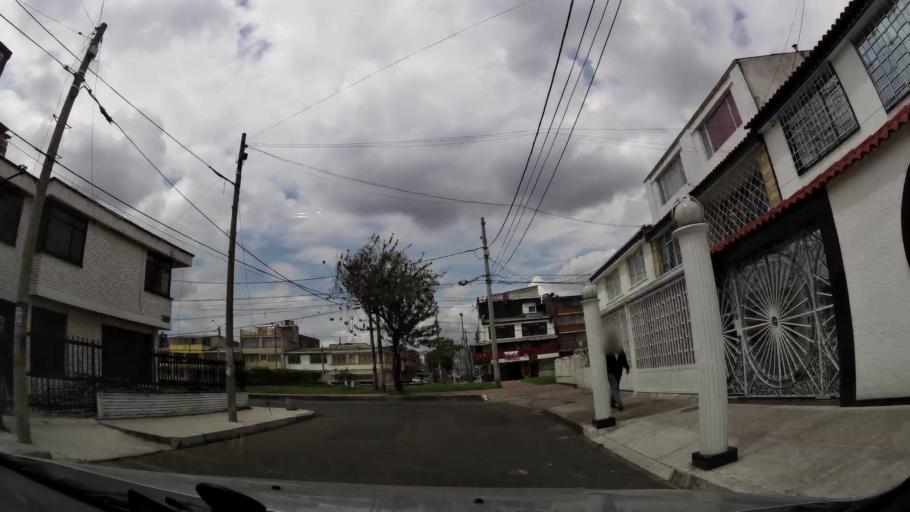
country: CO
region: Bogota D.C.
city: Bogota
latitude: 4.5987
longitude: -74.0993
